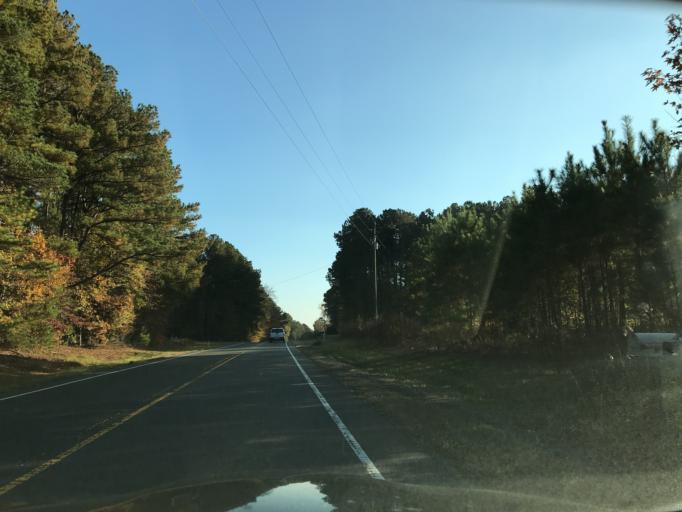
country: US
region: North Carolina
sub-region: Granville County
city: Creedmoor
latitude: 36.0080
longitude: -78.6873
